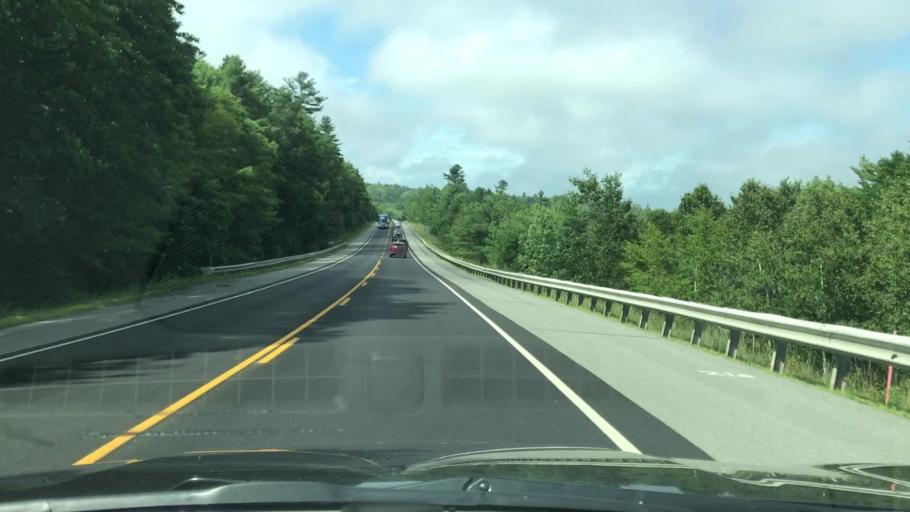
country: US
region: Maine
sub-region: Hancock County
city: Bucksport
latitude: 44.5471
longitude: -68.8091
